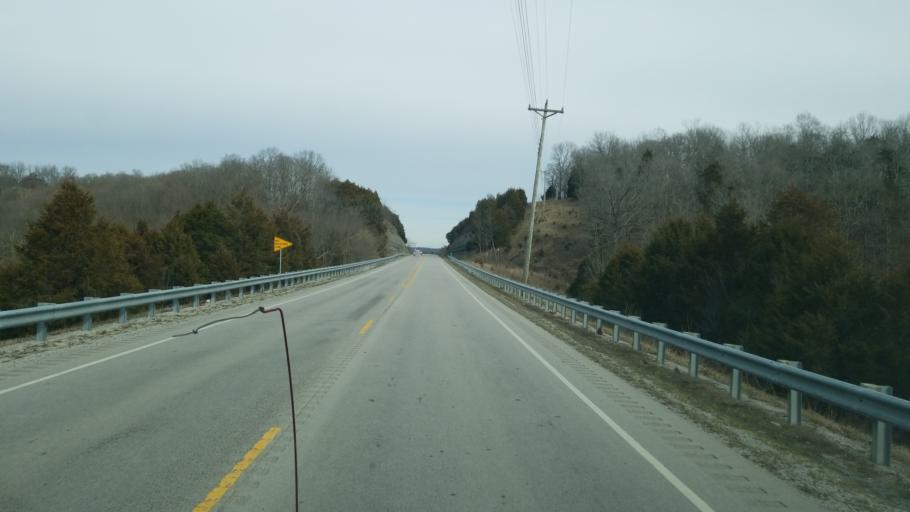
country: US
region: Kentucky
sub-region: Nicholas County
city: Carlisle
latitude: 38.4124
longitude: -84.0075
